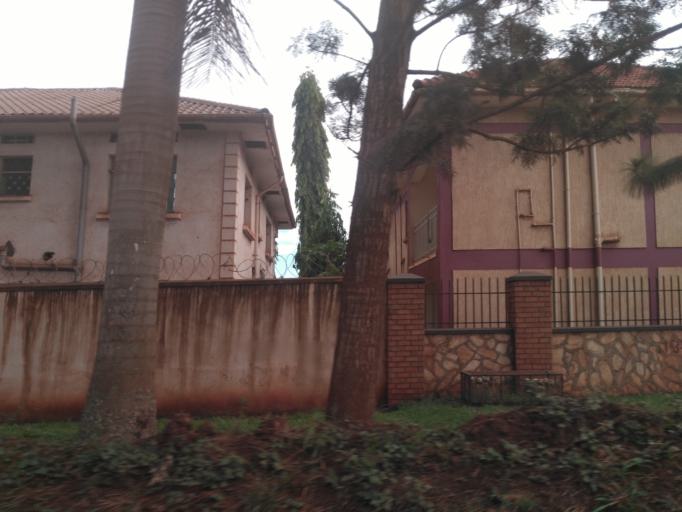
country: UG
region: Eastern Region
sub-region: Jinja District
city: Jinja
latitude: 0.4287
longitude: 33.1898
